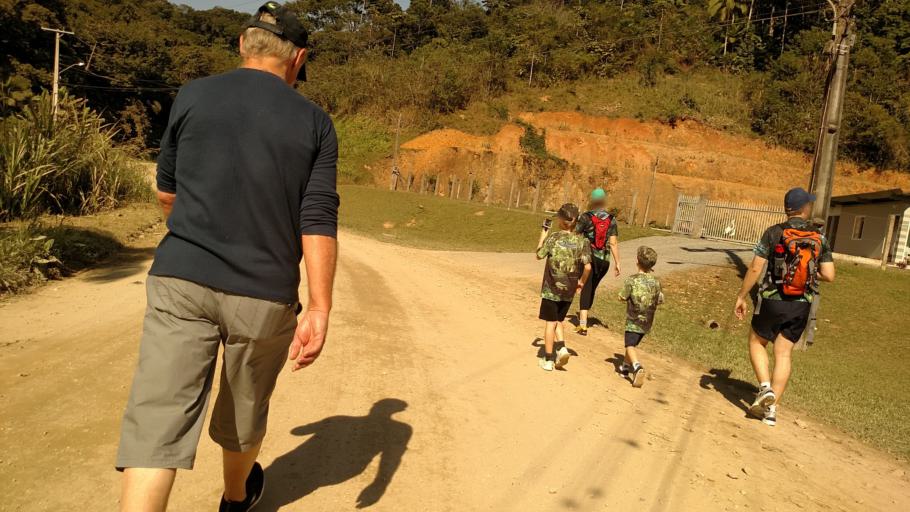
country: BR
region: Santa Catarina
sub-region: Pomerode
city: Pomerode
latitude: -26.7329
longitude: -49.0814
